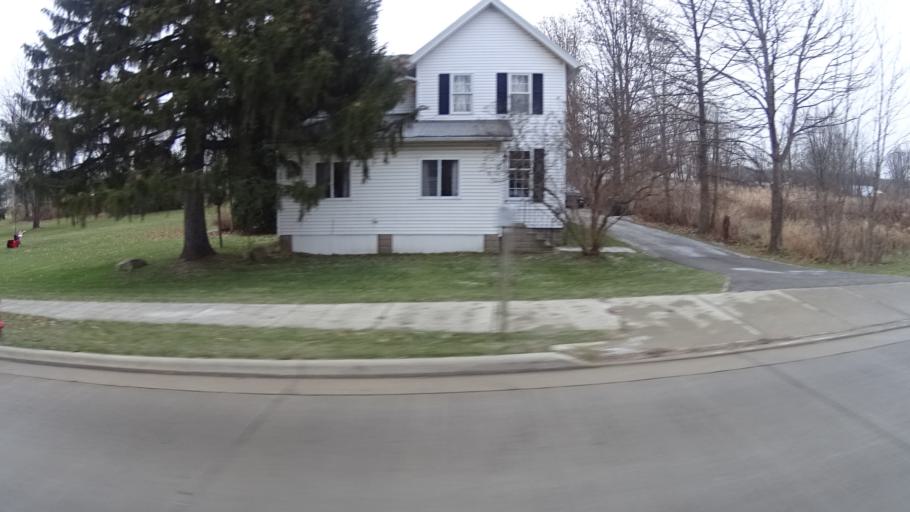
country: US
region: Ohio
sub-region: Lorain County
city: Grafton
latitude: 41.2806
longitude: -82.0513
